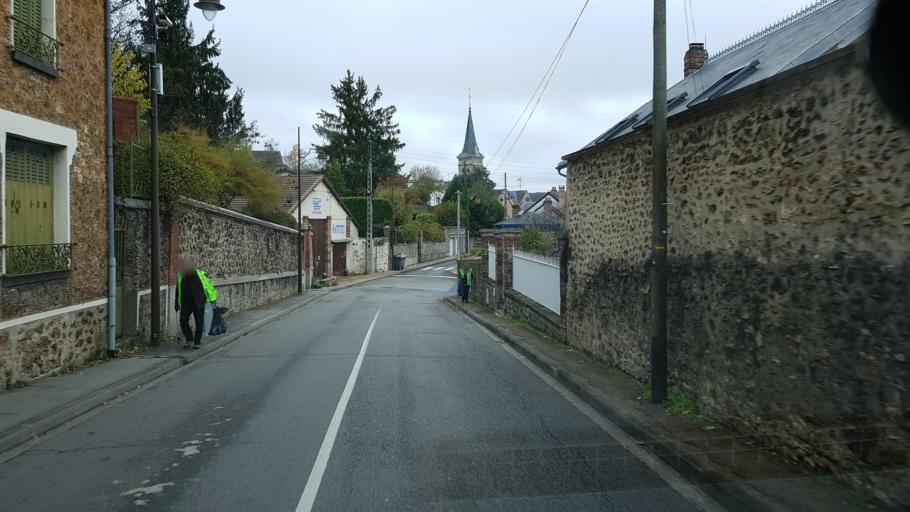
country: FR
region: Ile-de-France
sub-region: Departement des Yvelines
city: Chevreuse
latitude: 48.7097
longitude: 2.0375
